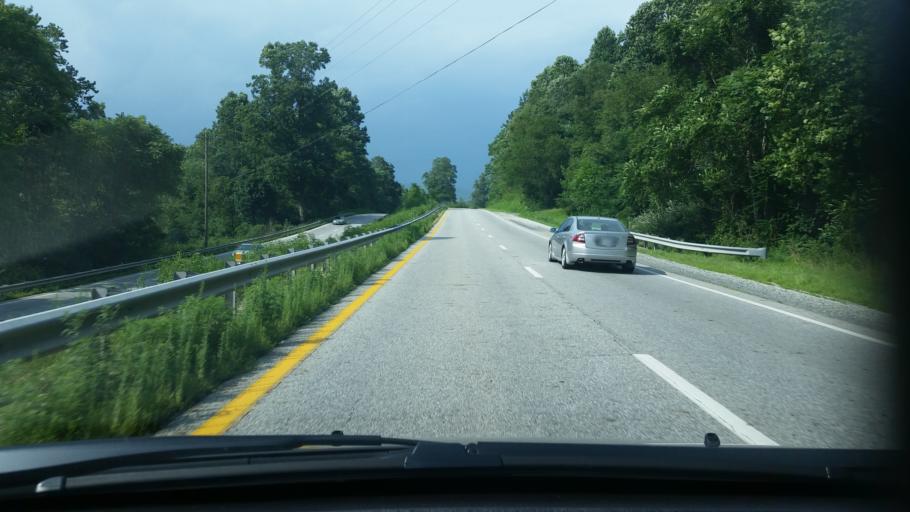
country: US
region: Virginia
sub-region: Nelson County
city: Lovingston
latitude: 37.7894
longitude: -78.8656
